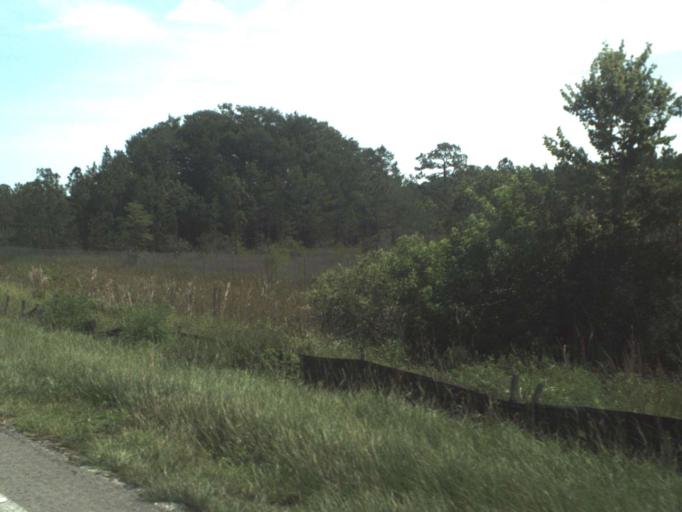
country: US
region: Florida
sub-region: Indian River County
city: Fellsmere
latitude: 27.8038
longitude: -80.5488
